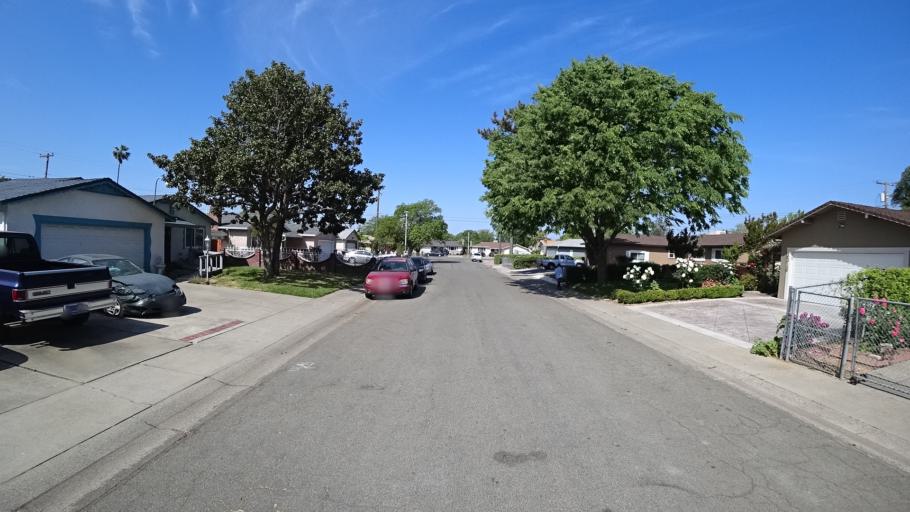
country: US
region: California
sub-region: Sacramento County
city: Parkway
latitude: 38.5079
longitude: -121.4851
